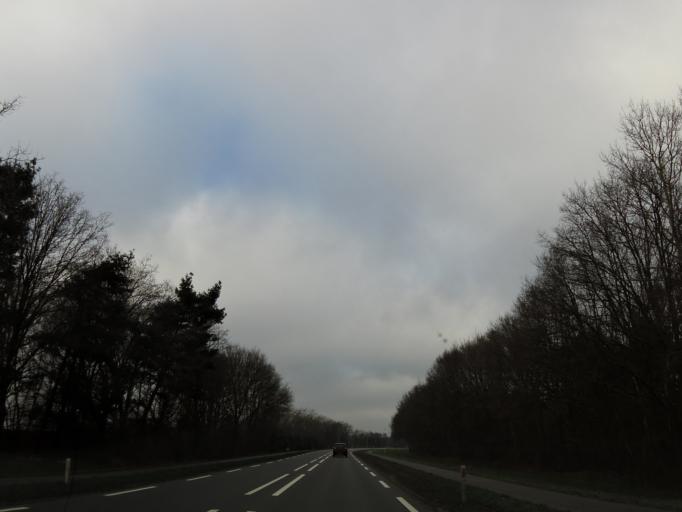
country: NL
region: Limburg
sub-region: Gemeente Venray
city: Venray
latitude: 51.4552
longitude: 5.9448
